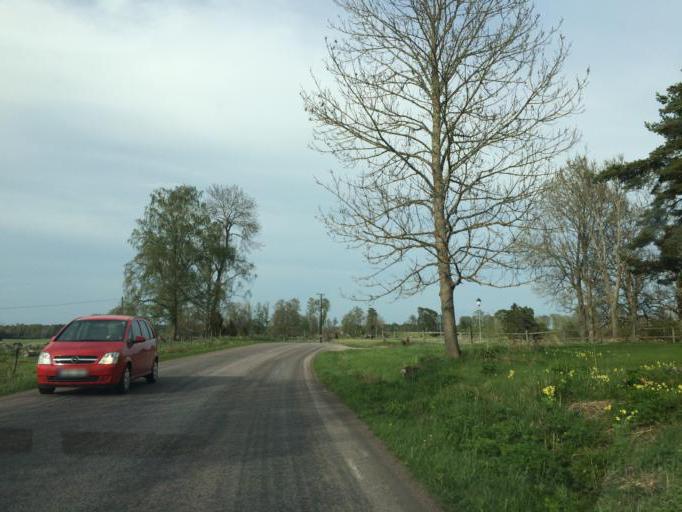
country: SE
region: Vaestmanland
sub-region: Hallstahammars Kommun
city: Hallstahammar
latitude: 59.6016
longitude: 16.1869
